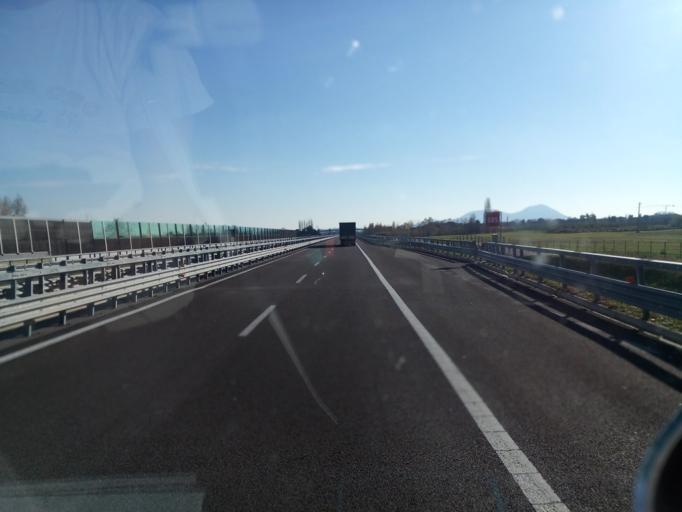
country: IT
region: Veneto
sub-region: Provincia di Vicenza
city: Longare
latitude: 45.4923
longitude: 11.6199
